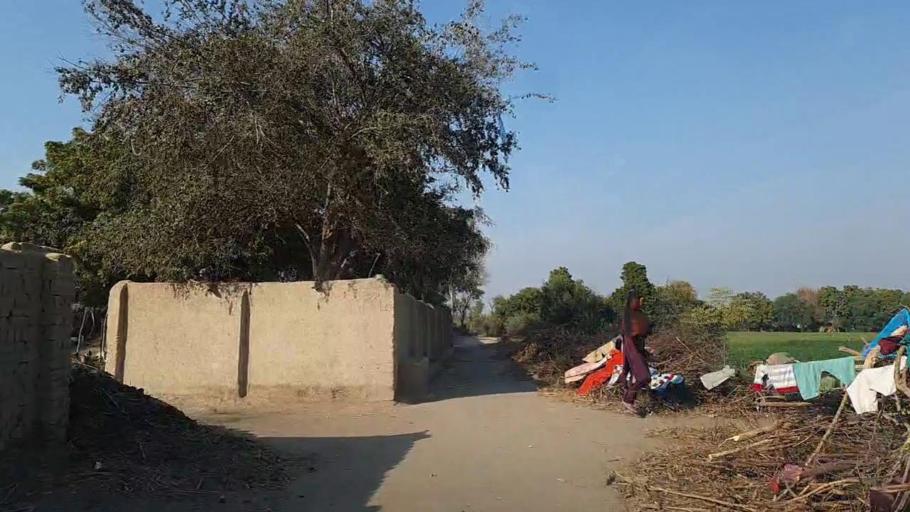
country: PK
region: Sindh
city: Nawabshah
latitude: 26.3771
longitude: 68.4776
